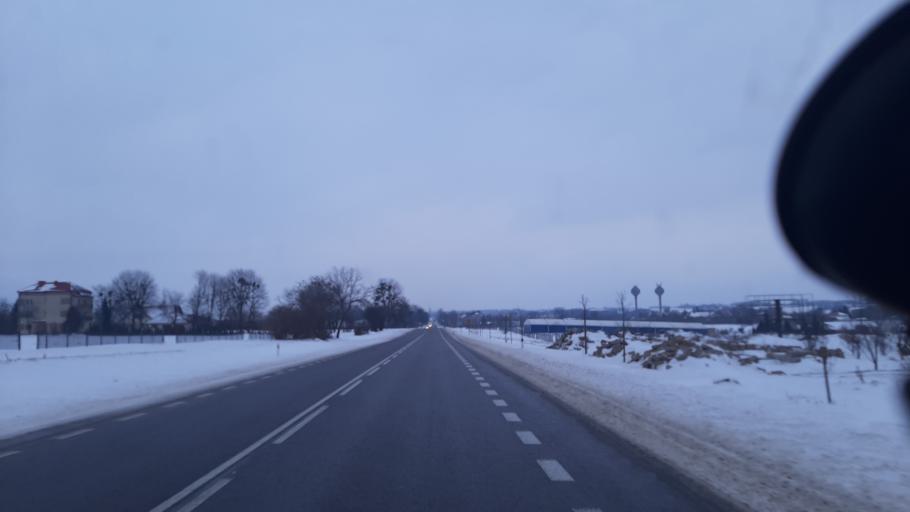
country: PL
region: Lublin Voivodeship
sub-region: Powiat pulawski
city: Markuszow
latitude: 51.3678
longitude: 22.2860
